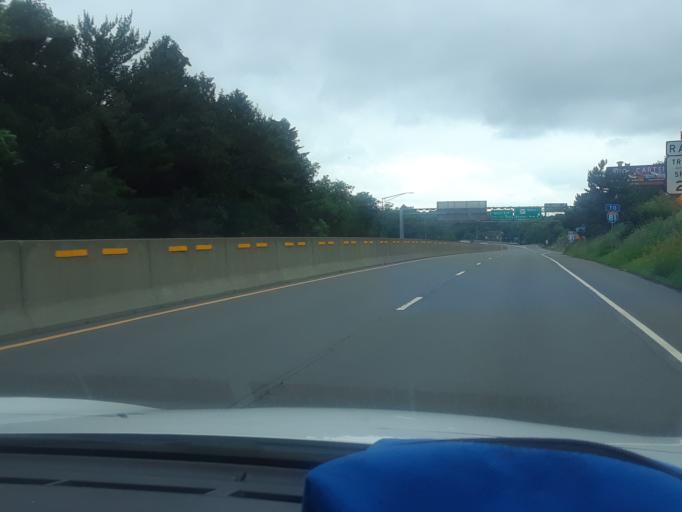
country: US
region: Pennsylvania
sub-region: Lackawanna County
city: Chinchilla
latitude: 41.4491
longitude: -75.6689
